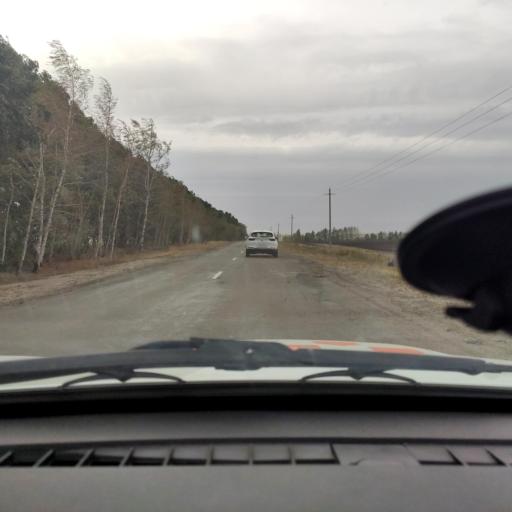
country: RU
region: Lipetsk
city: Khlevnoye
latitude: 52.0058
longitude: 39.1370
